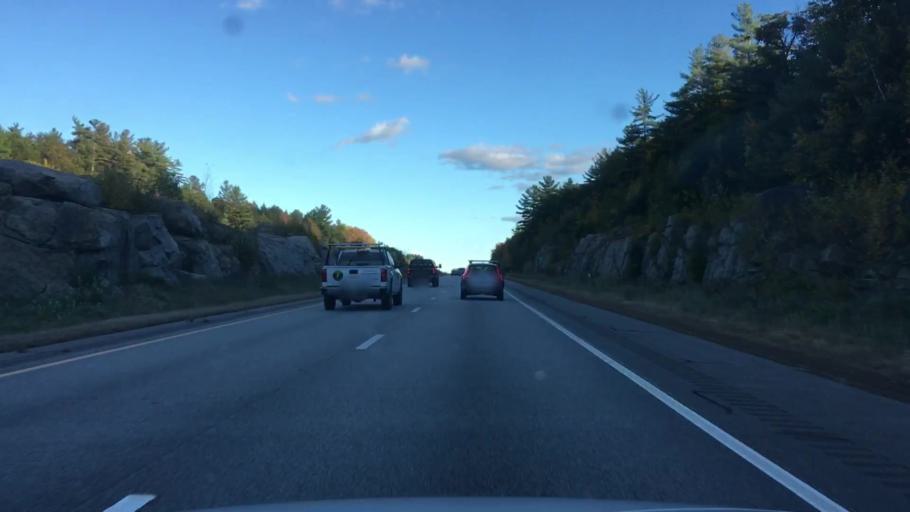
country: US
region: New Hampshire
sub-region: Rockingham County
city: Candia
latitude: 43.0310
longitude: -71.2494
